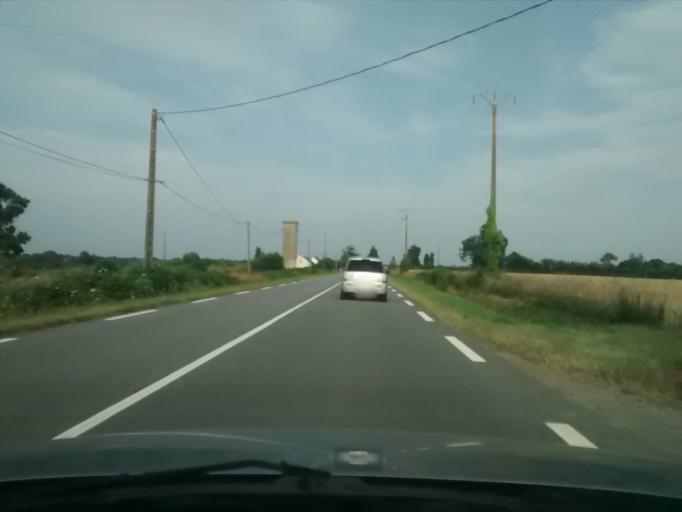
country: FR
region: Brittany
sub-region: Departement d'Ille-et-Vilaine
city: Erbree
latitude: 48.1166
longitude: -1.1485
